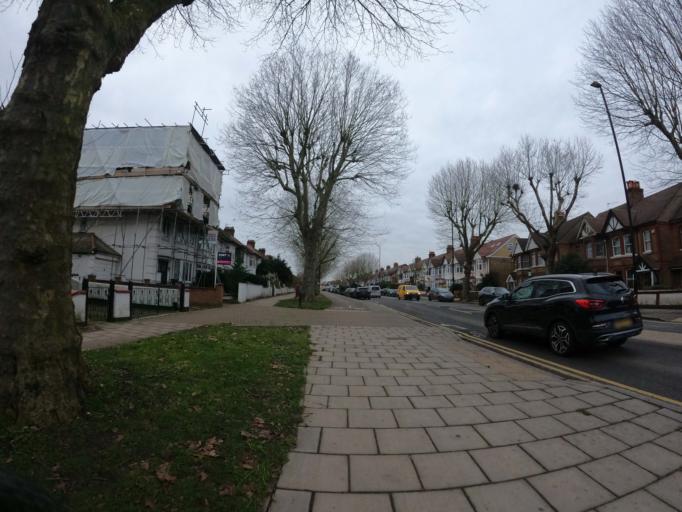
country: GB
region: England
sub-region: Greater London
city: Brentford
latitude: 51.4936
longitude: -0.3194
